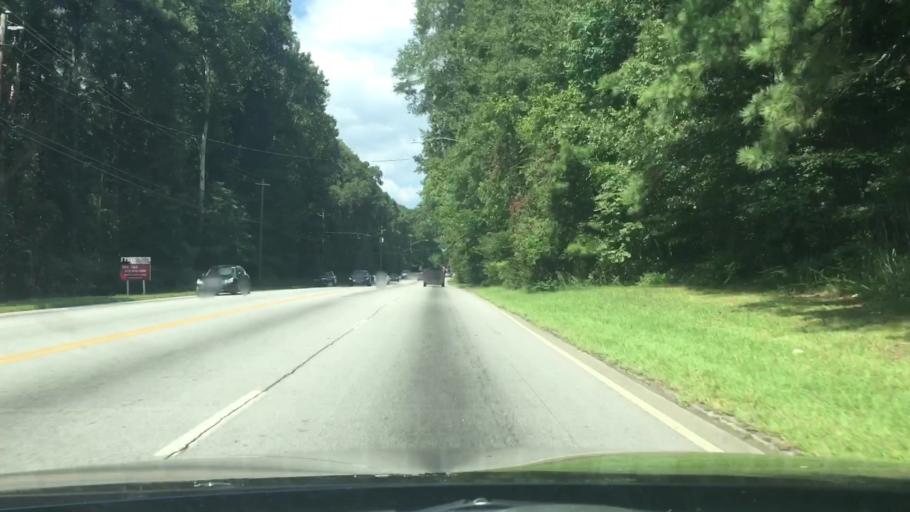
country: US
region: Georgia
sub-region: DeKalb County
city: Lithonia
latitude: 33.7095
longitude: -84.1290
